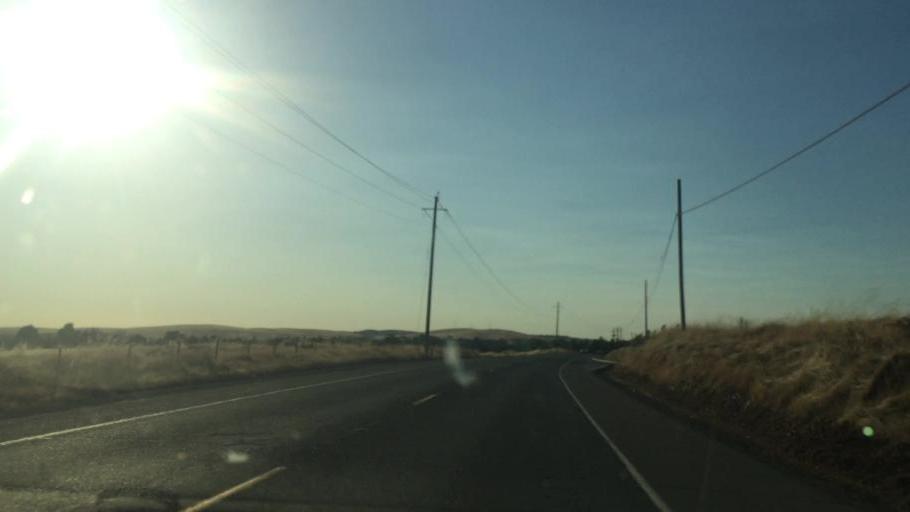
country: US
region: California
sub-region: El Dorado County
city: El Dorado Hills
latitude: 38.6167
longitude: -121.0487
